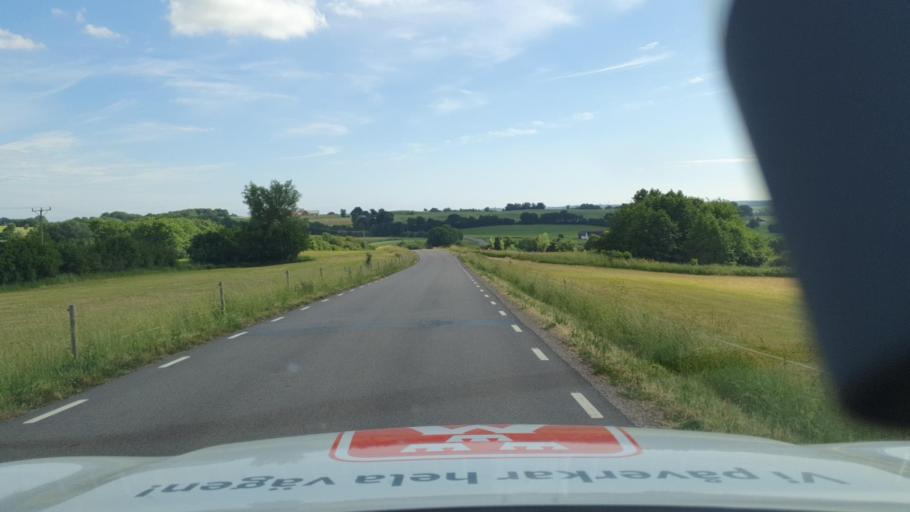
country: SE
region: Skane
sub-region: Sjobo Kommun
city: Blentarp
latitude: 55.5346
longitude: 13.5487
